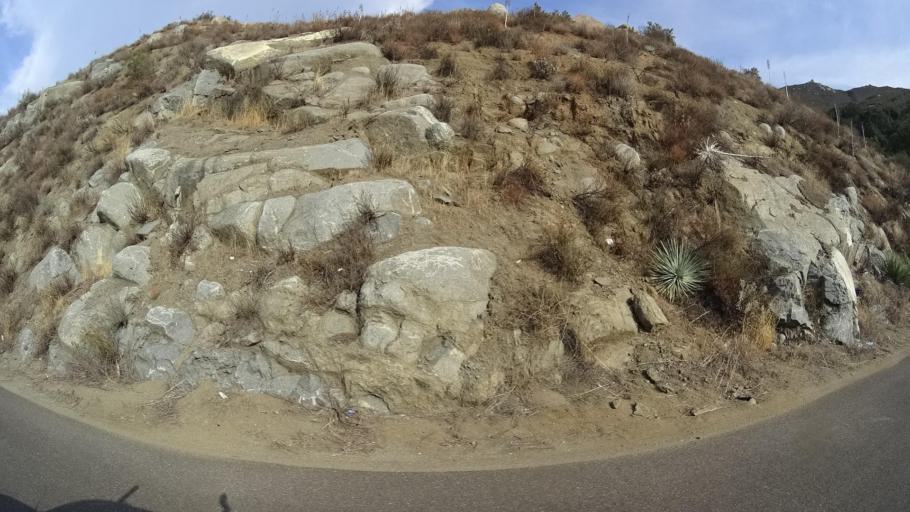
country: US
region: California
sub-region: San Diego County
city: San Pasqual
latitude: 33.0833
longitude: -116.9166
